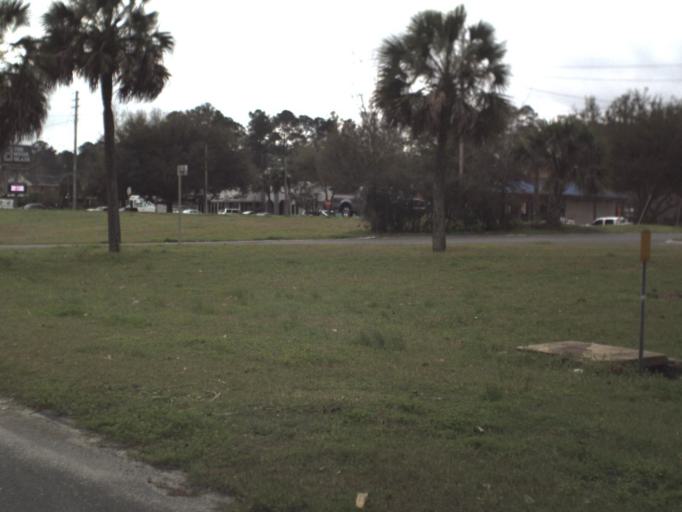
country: US
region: Florida
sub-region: Leon County
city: Tallahassee
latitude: 30.4352
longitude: -84.2575
